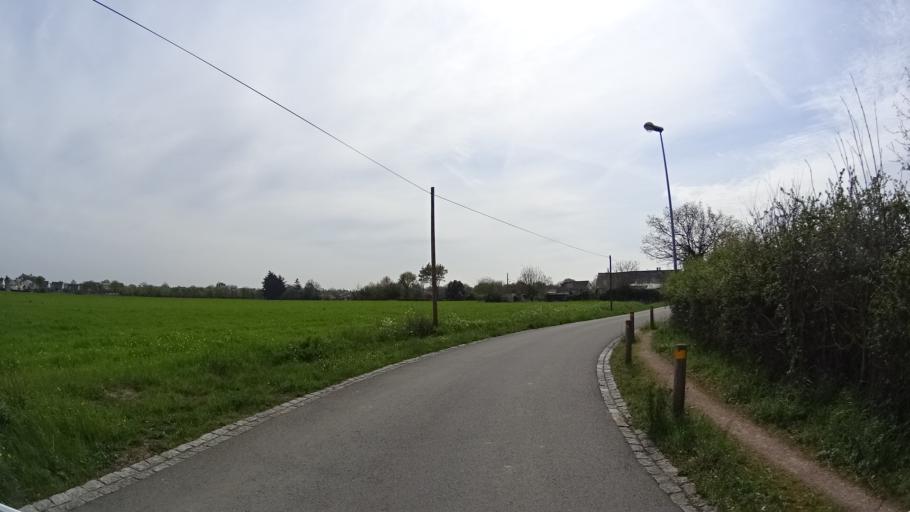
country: FR
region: Brittany
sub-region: Departement d'Ille-et-Vilaine
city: Chartres-de-Bretagne
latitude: 48.0347
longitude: -1.7191
